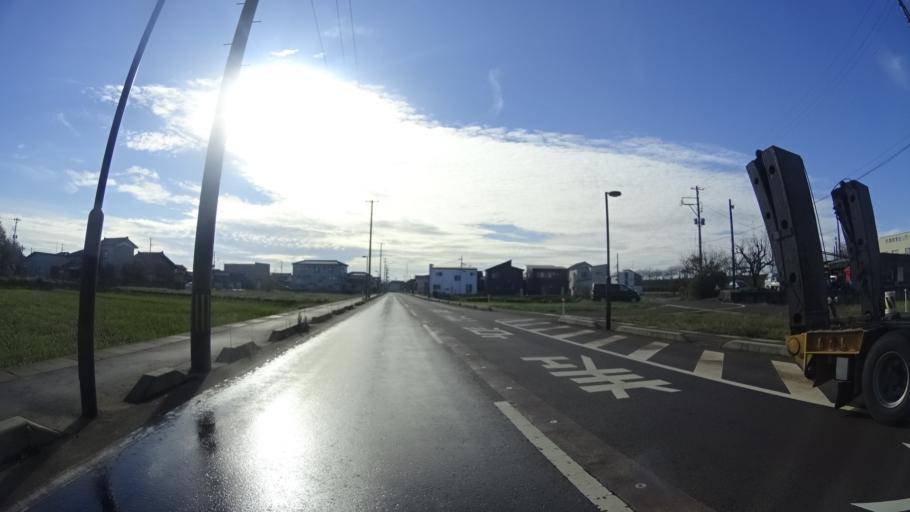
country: JP
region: Niigata
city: Yoshida-kasugacho
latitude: 37.6263
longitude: 138.8372
